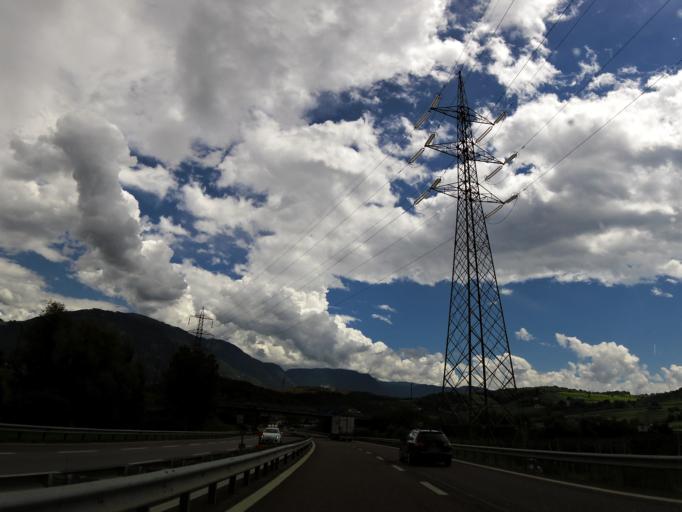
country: IT
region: Trentino-Alto Adige
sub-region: Bolzano
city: Cornaiano
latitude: 46.4869
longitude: 11.2885
